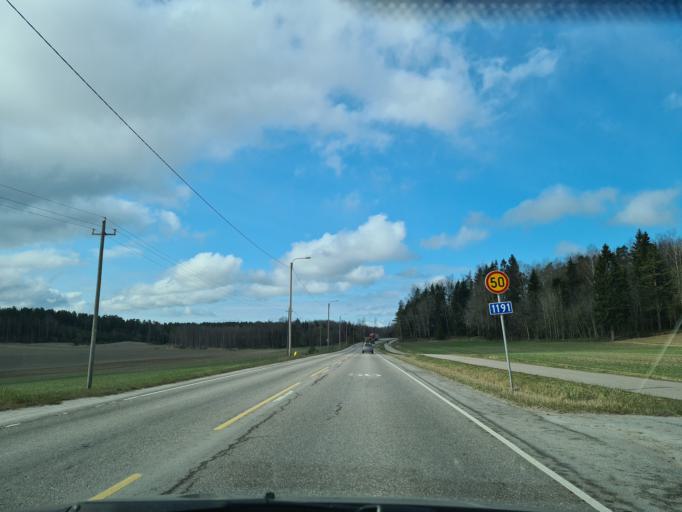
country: FI
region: Uusimaa
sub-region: Helsinki
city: Kirkkonummi
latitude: 60.1054
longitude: 24.4370
